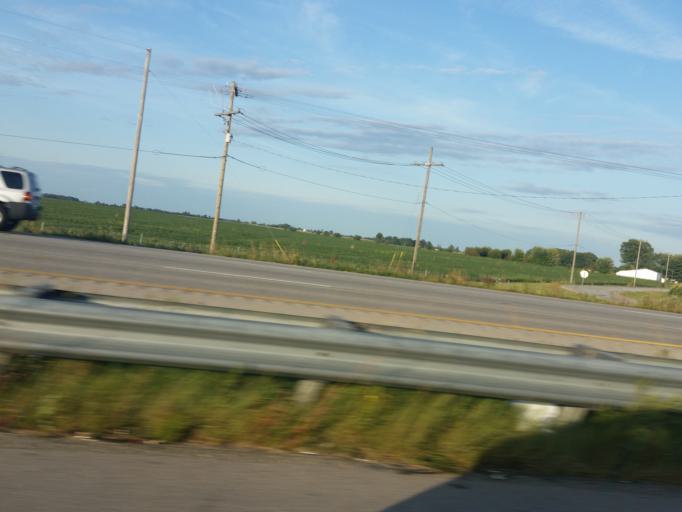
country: US
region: Indiana
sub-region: Boone County
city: Dale
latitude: 39.9962
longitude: -86.4141
